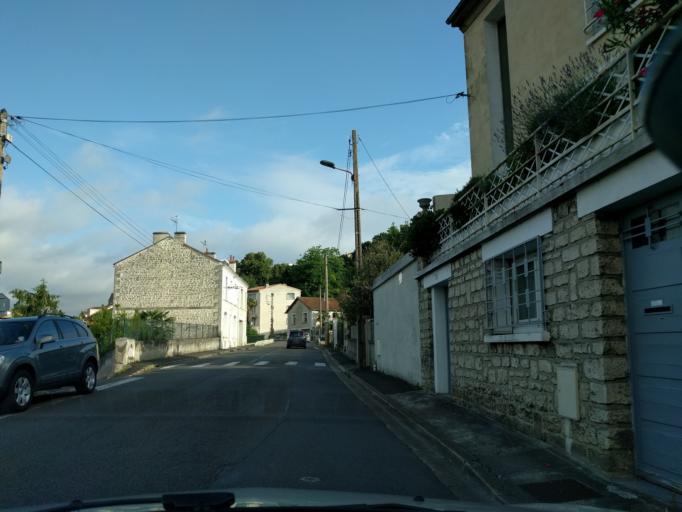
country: FR
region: Poitou-Charentes
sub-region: Departement de la Charente
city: Angouleme
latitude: 45.6470
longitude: 0.1506
